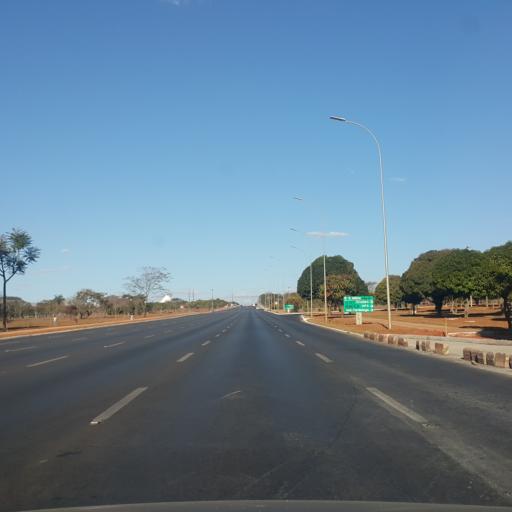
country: BR
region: Federal District
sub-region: Brasilia
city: Brasilia
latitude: -15.7791
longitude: -47.9327
